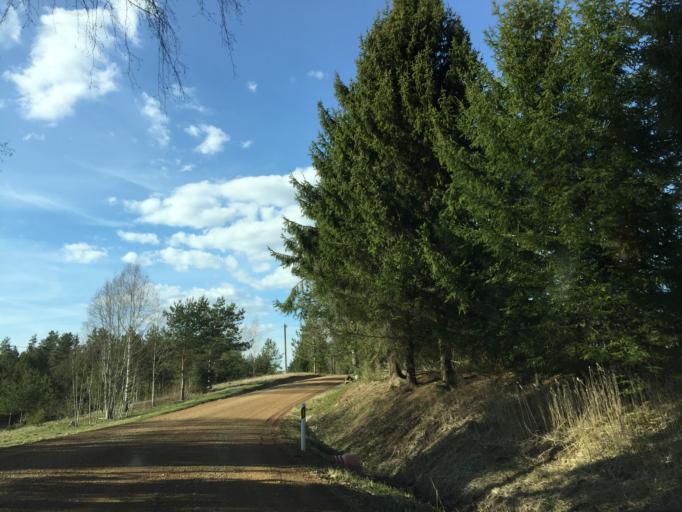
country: EE
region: Tartu
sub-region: Elva linn
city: Elva
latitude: 58.0902
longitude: 26.5136
